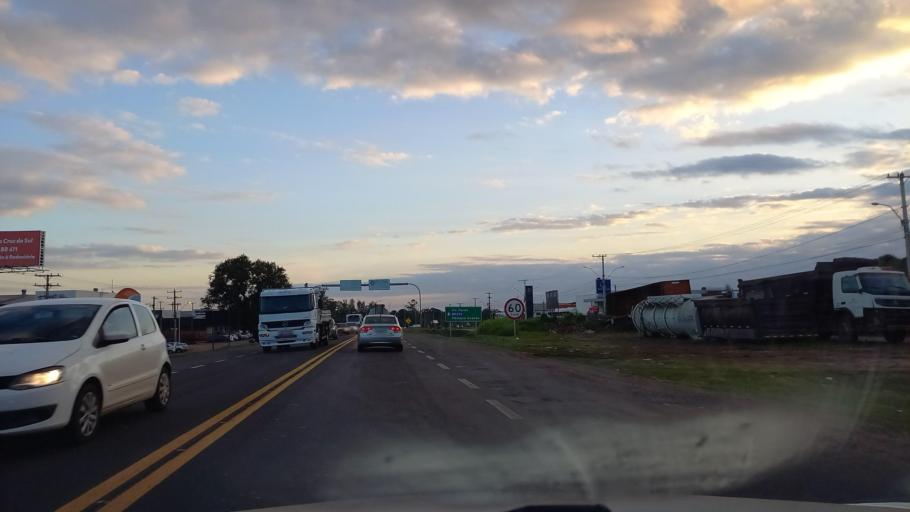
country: BR
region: Rio Grande do Sul
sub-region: Santa Cruz Do Sul
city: Santa Cruz do Sul
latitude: -29.6871
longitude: -52.4464
